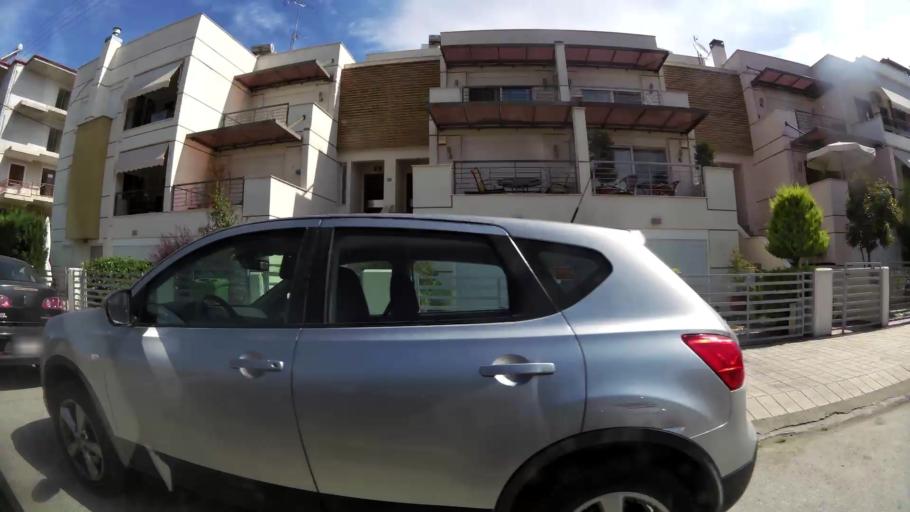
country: GR
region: Central Macedonia
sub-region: Nomos Pierias
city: Katerini
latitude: 40.2750
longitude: 22.4857
